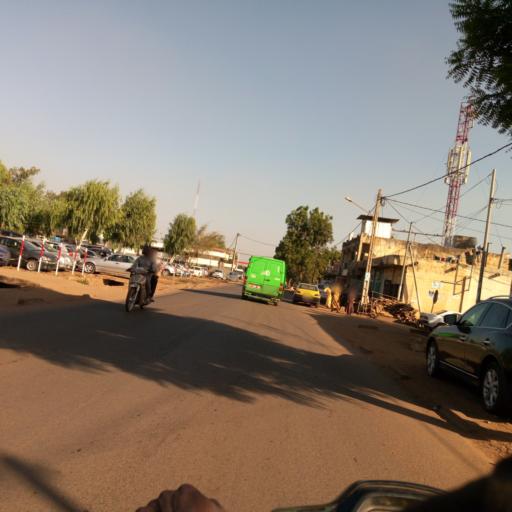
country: ML
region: Bamako
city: Bamako
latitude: 12.6532
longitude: -8.0189
